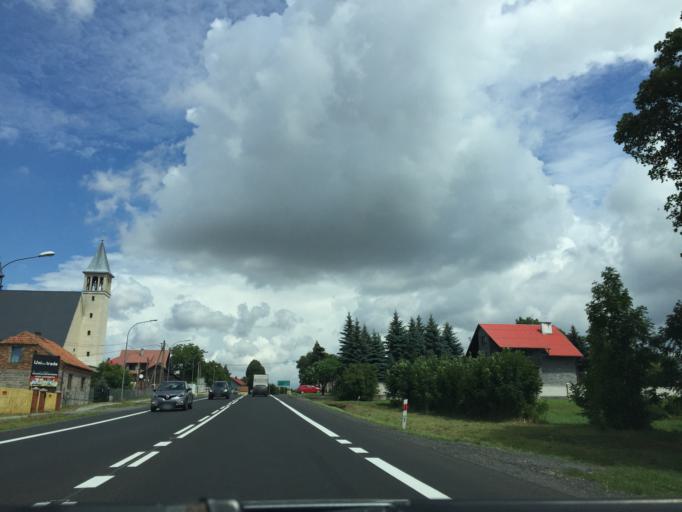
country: PL
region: Lesser Poland Voivodeship
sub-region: Powiat krakowski
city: Michalowice
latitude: 50.2018
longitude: 20.0115
